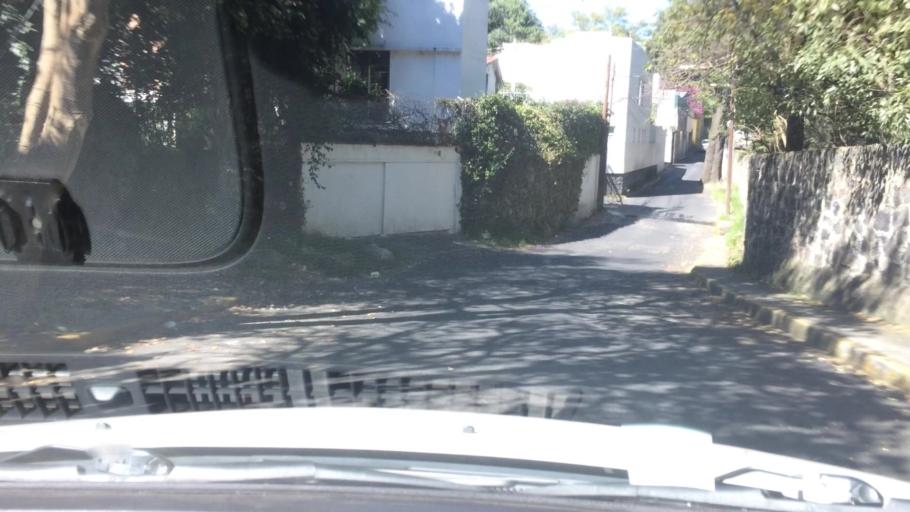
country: MX
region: Mexico City
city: Magdalena Contreras
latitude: 19.3241
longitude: -99.2208
